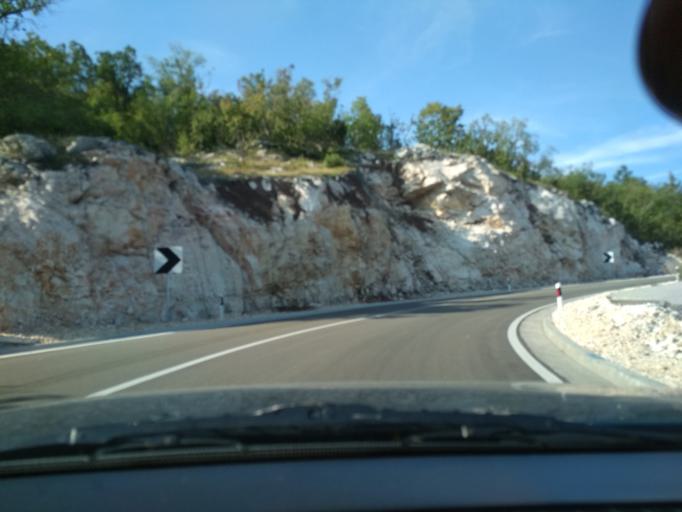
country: ME
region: Cetinje
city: Cetinje
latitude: 42.4090
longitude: 18.8870
